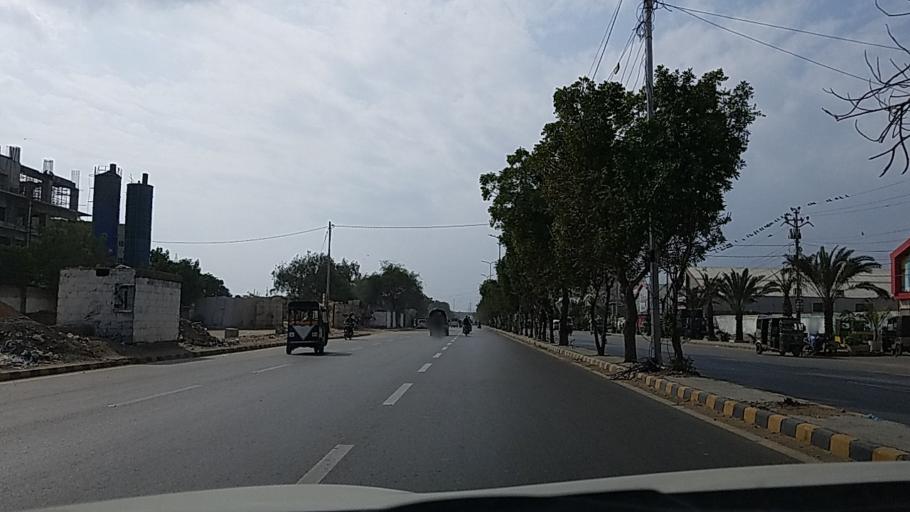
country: PK
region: Sindh
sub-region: Karachi District
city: Karachi
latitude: 24.8181
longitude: 67.1132
